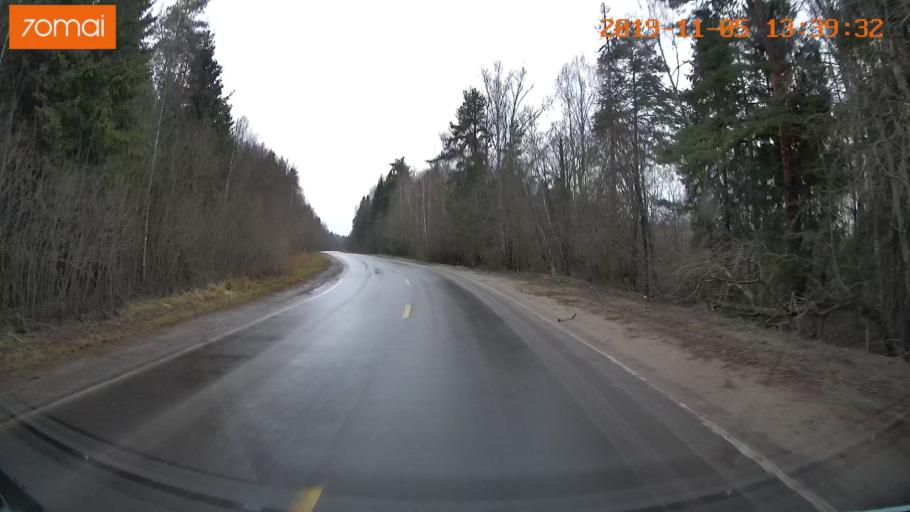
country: RU
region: Ivanovo
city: Shuya
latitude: 56.9405
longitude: 41.3864
